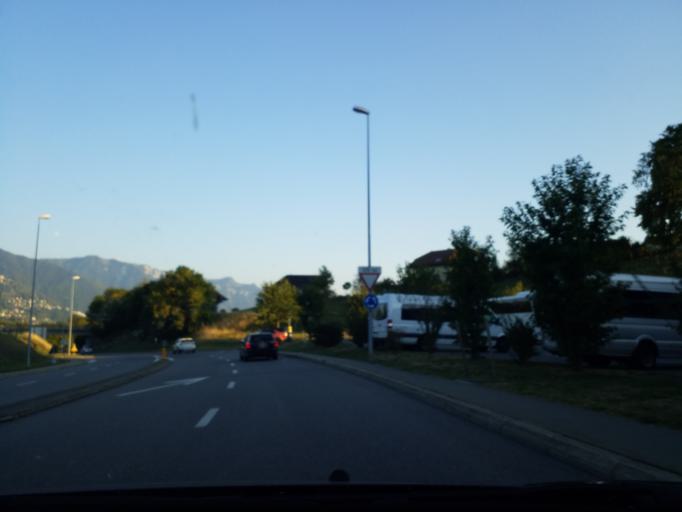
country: CH
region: Vaud
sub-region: Riviera-Pays-d'Enhaut District
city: La Tour-de-Peilz
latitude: 46.4691
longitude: 6.8633
